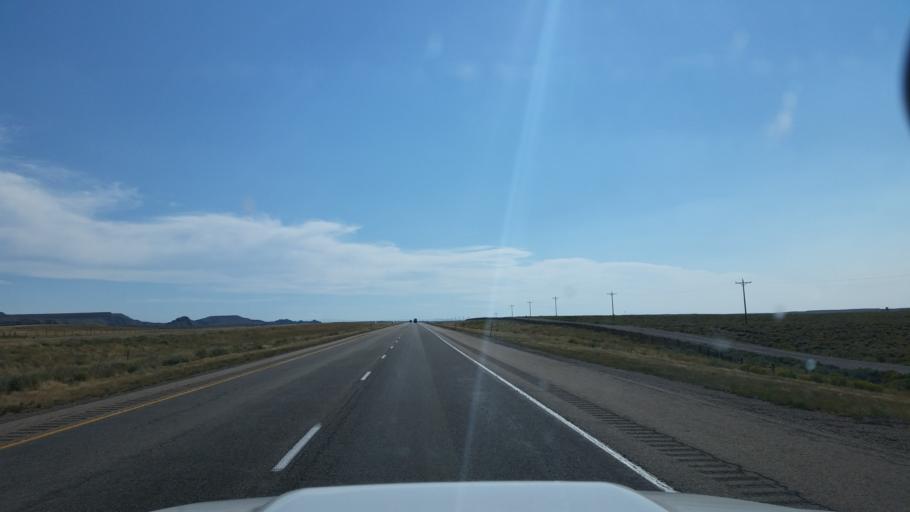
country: US
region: Wyoming
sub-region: Uinta County
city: Lyman
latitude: 41.4506
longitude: -110.0743
